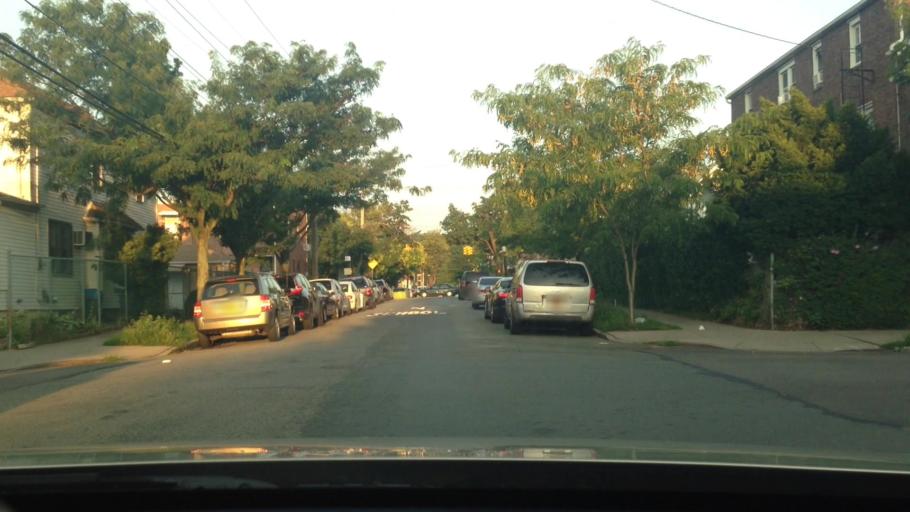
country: US
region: New York
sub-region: Queens County
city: Borough of Queens
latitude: 40.7385
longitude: -73.8654
